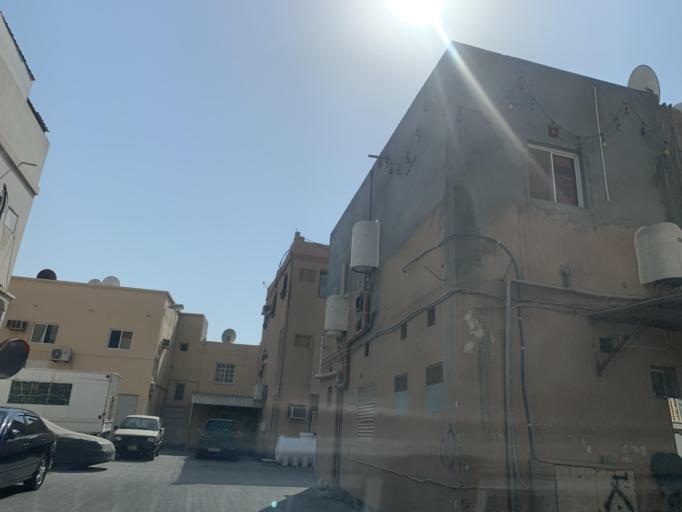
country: BH
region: Manama
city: Jidd Hafs
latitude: 26.2041
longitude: 50.5312
